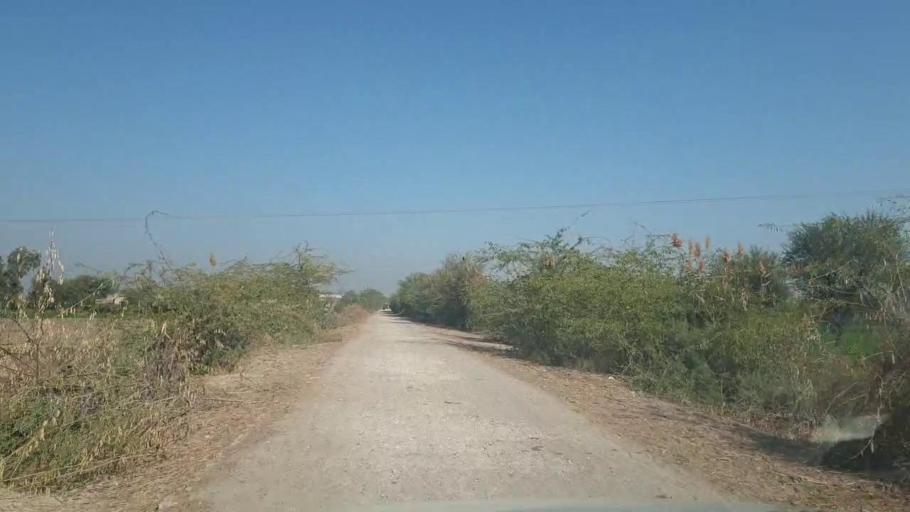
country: PK
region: Sindh
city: Mirpur Khas
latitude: 25.5033
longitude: 69.1380
